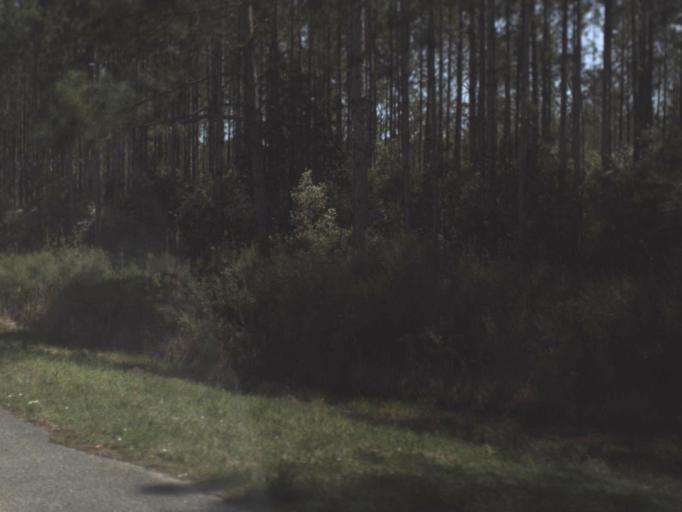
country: US
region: Florida
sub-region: Franklin County
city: Apalachicola
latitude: 29.7286
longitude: -85.1339
